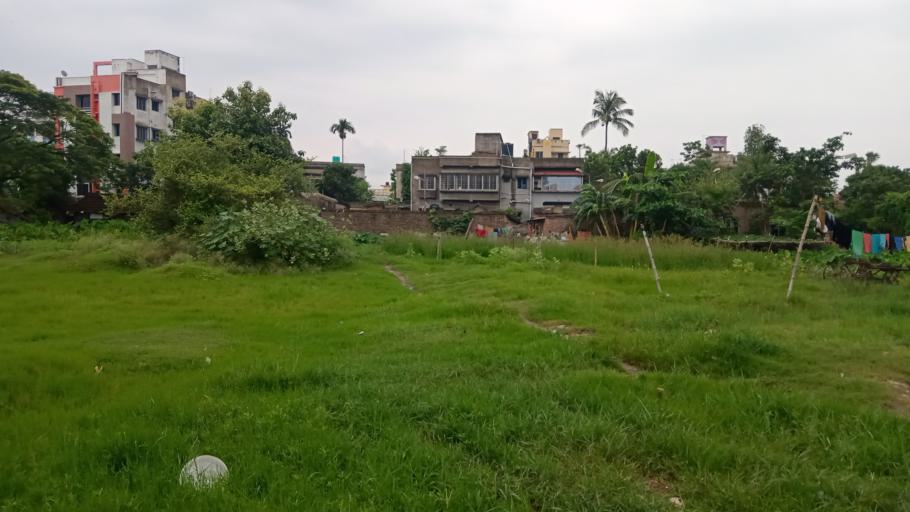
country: IN
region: West Bengal
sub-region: Kolkata
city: Kolkata
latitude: 22.4667
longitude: 88.3882
